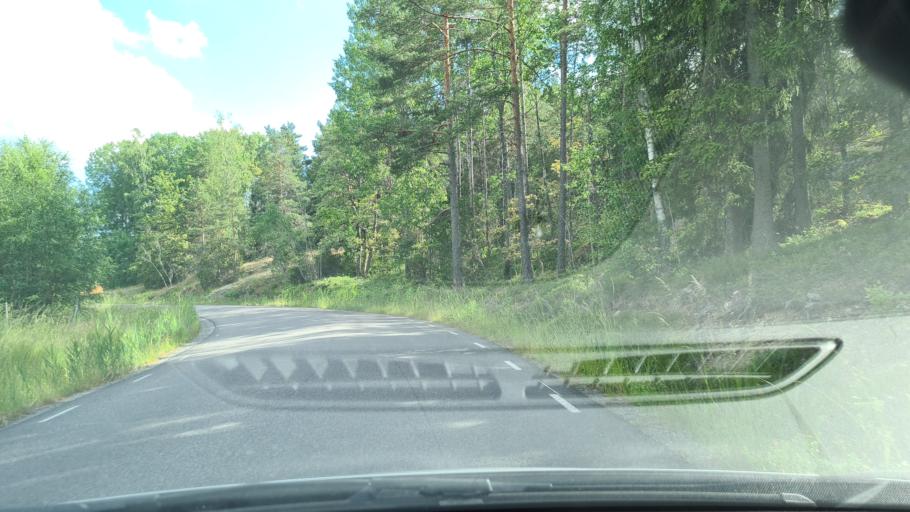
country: SE
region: Stockholm
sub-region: Varmdo Kommun
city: Mortnas
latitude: 59.3970
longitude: 18.4651
